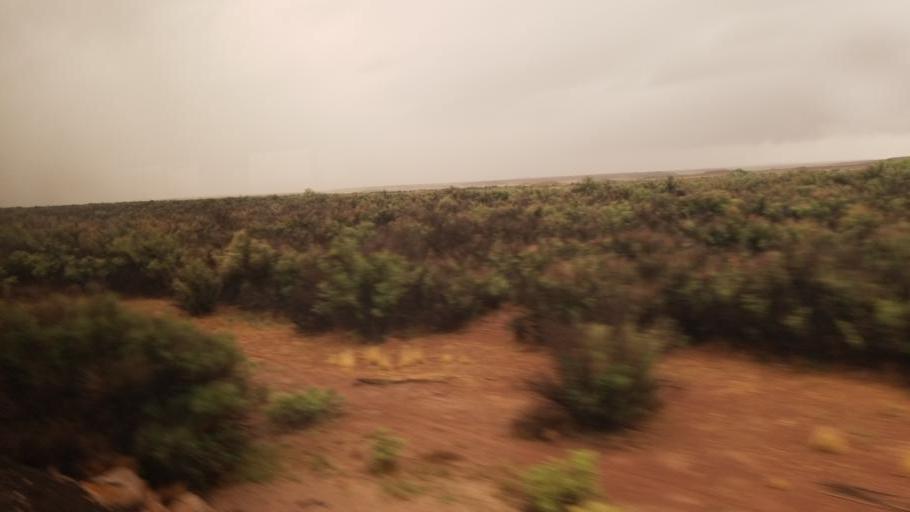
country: US
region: Arizona
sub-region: Navajo County
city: Joseph City
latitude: 34.9589
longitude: -110.3770
